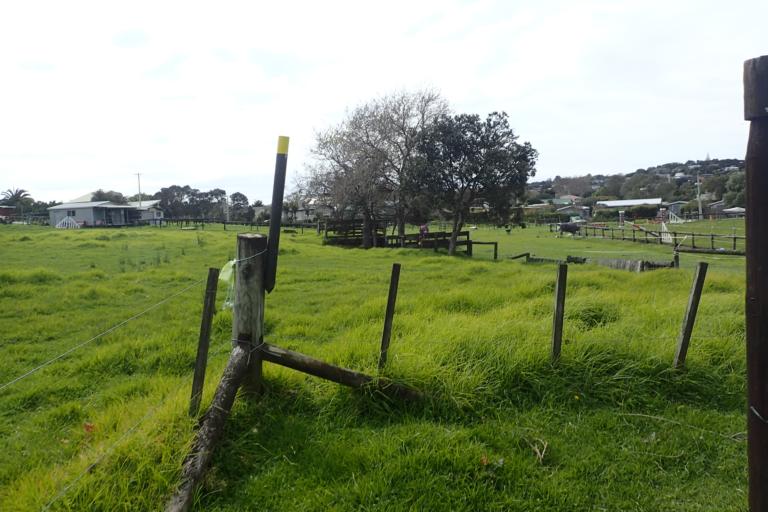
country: NZ
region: Auckland
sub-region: Auckland
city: Pakuranga
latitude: -36.7896
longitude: 175.0079
